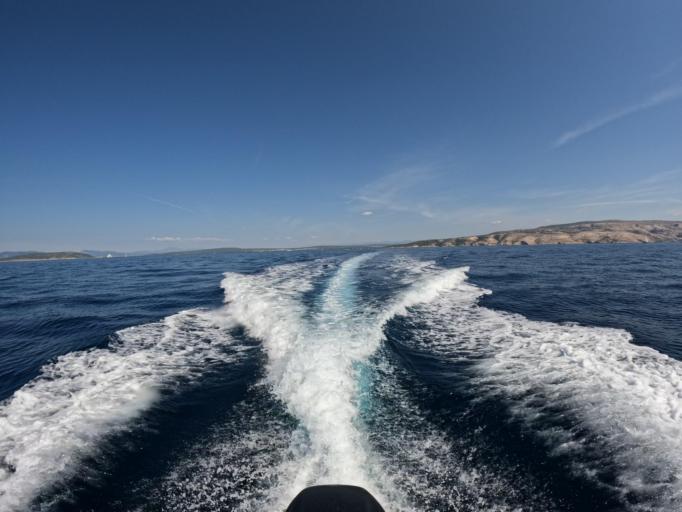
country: HR
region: Primorsko-Goranska
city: Punat
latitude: 44.9373
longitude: 14.6160
